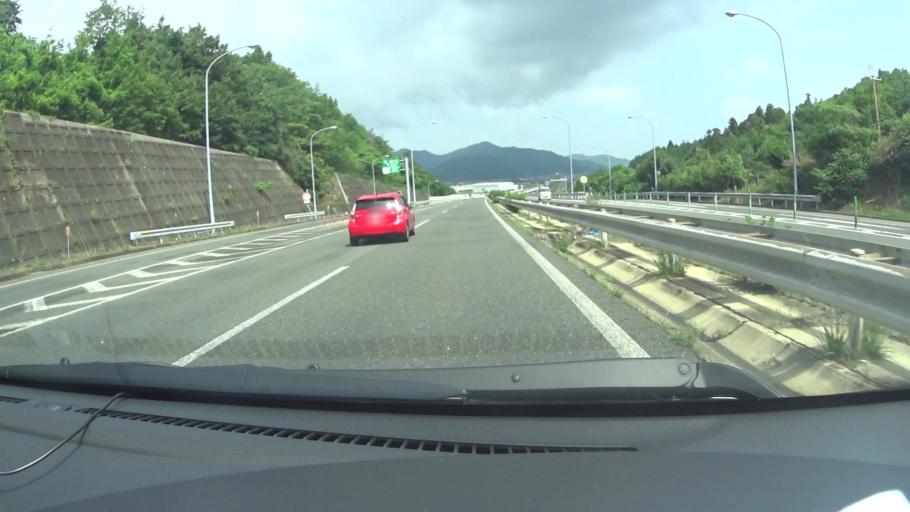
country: JP
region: Kyoto
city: Kameoka
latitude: 35.0056
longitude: 135.5645
